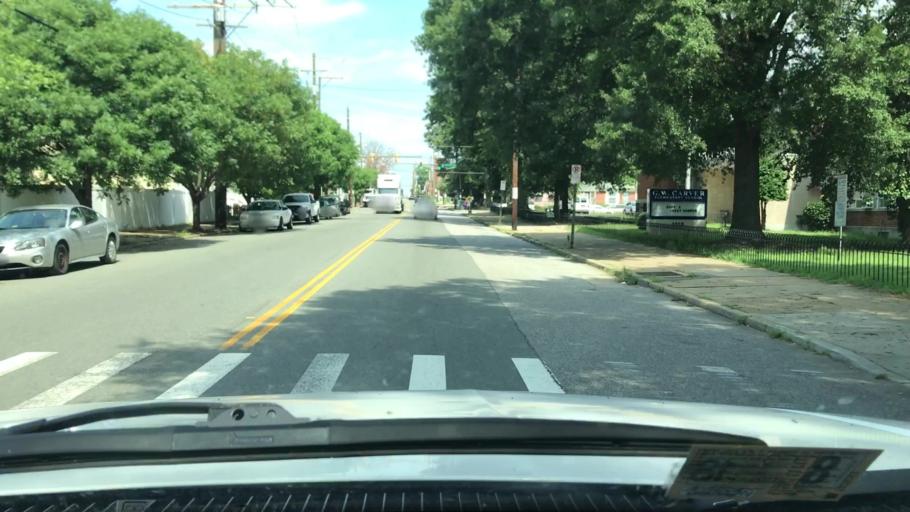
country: US
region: Virginia
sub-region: City of Richmond
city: Richmond
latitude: 37.5541
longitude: -77.4486
